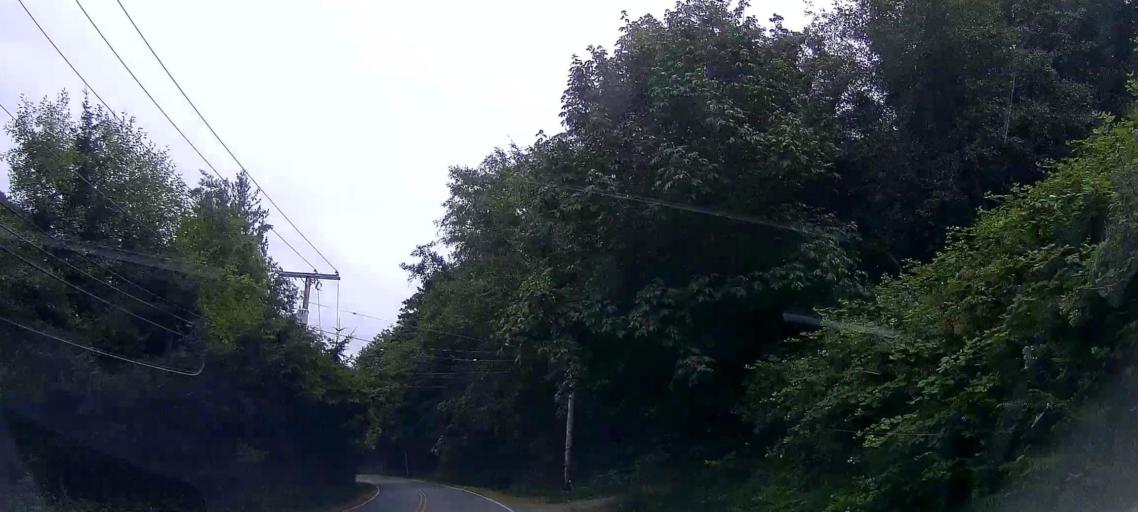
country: US
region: Washington
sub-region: Skagit County
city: Anacortes
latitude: 48.4490
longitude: -122.6417
